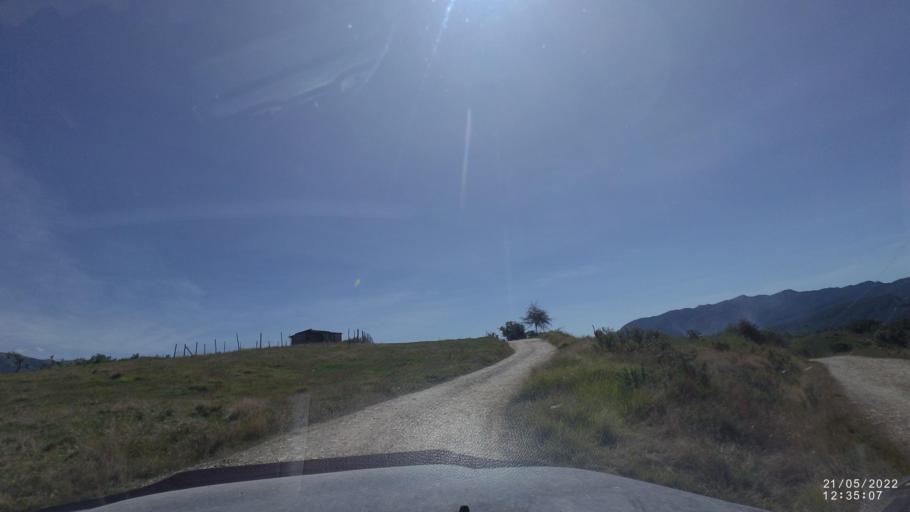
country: BO
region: Cochabamba
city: Colomi
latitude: -17.2050
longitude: -65.9148
